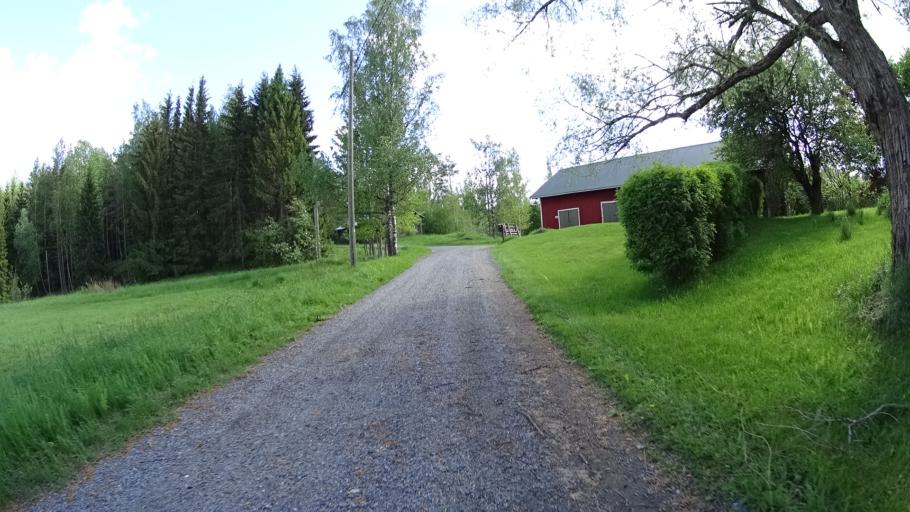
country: FI
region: Varsinais-Suomi
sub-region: Salo
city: Kisko
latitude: 60.1968
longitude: 23.5480
